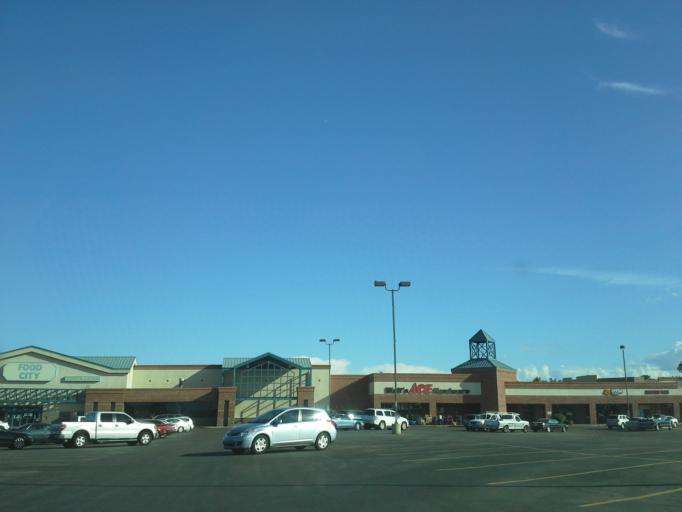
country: US
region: Arizona
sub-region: Maricopa County
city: Phoenix
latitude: 33.4959
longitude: -112.1012
